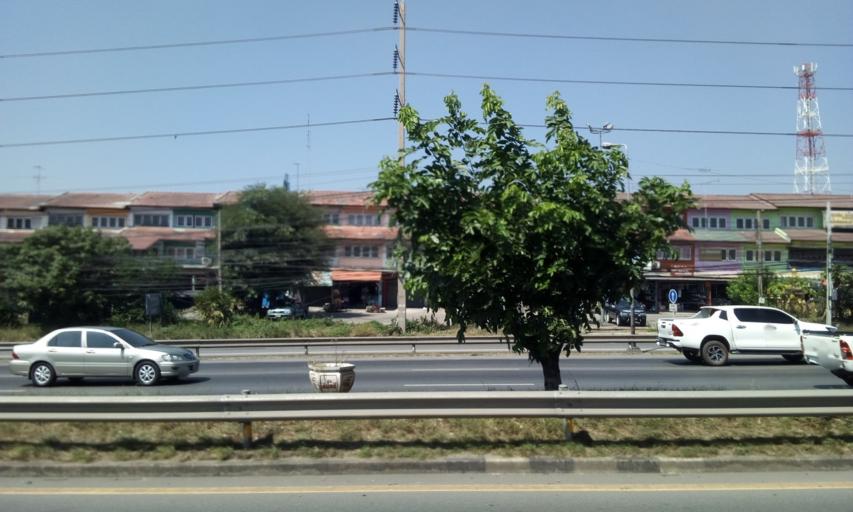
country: TH
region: Sara Buri
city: Kaeng Khoi
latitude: 14.6084
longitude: 101.0691
